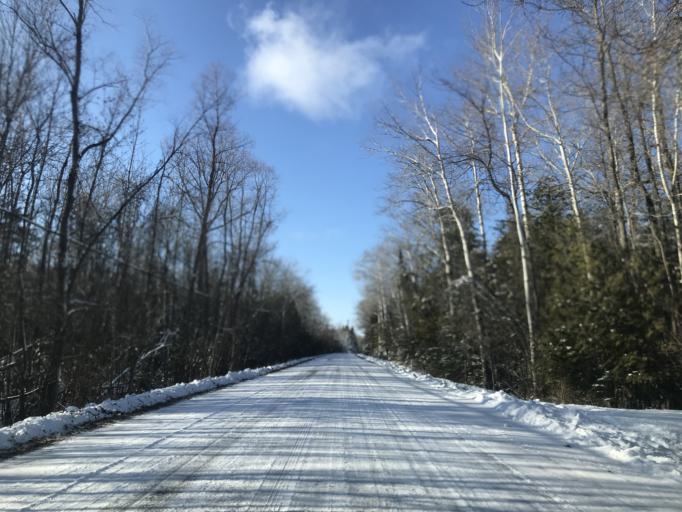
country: US
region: Wisconsin
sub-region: Door County
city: Sturgeon Bay
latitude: 44.8492
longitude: -87.5068
